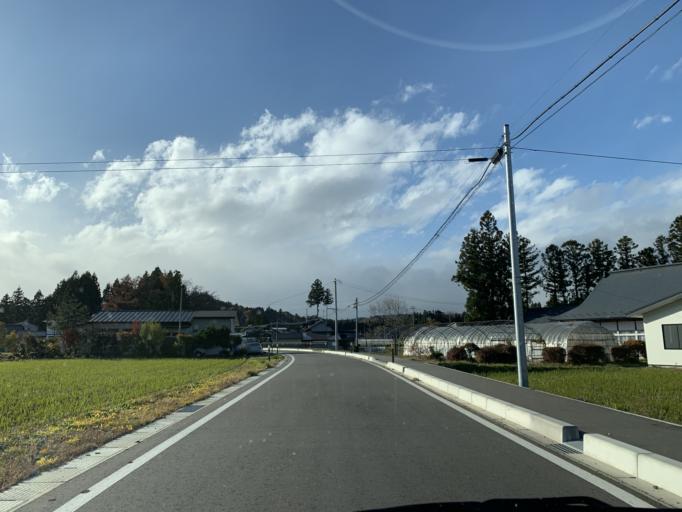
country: JP
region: Iwate
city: Ichinoseki
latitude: 39.0080
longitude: 141.0987
